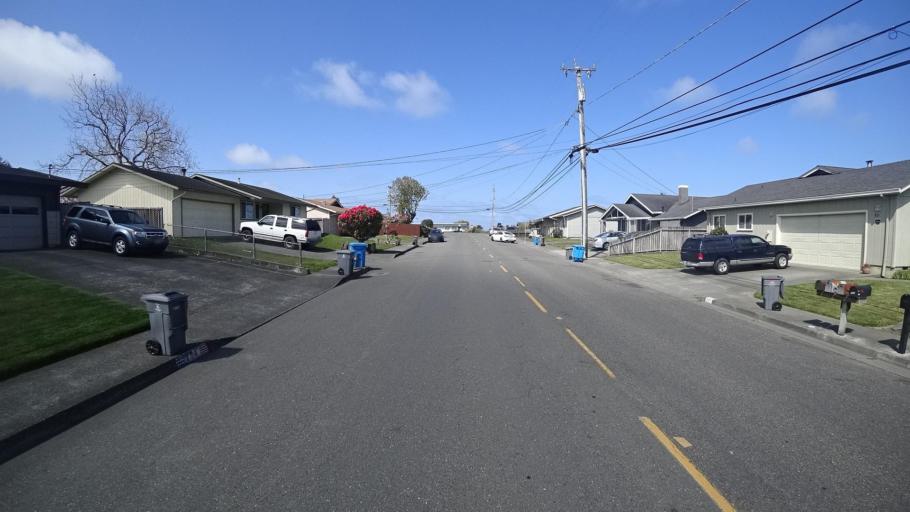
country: US
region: California
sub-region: Humboldt County
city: Bayview
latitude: 40.7608
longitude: -124.1800
